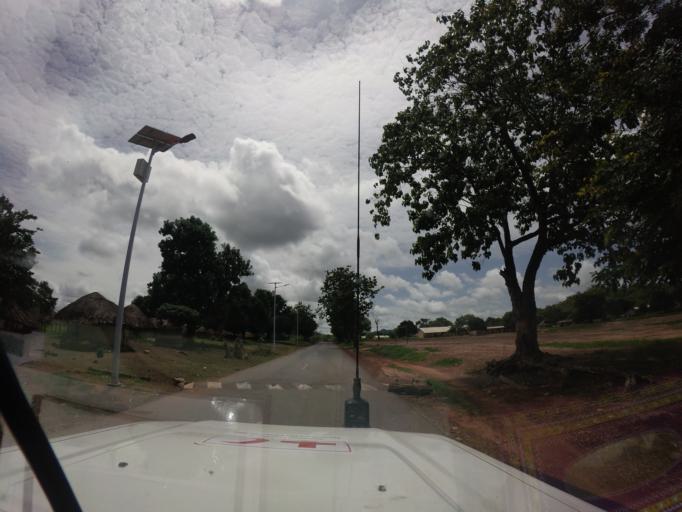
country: SL
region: Northern Province
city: Gberia Fotombu
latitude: 10.0702
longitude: -11.1203
